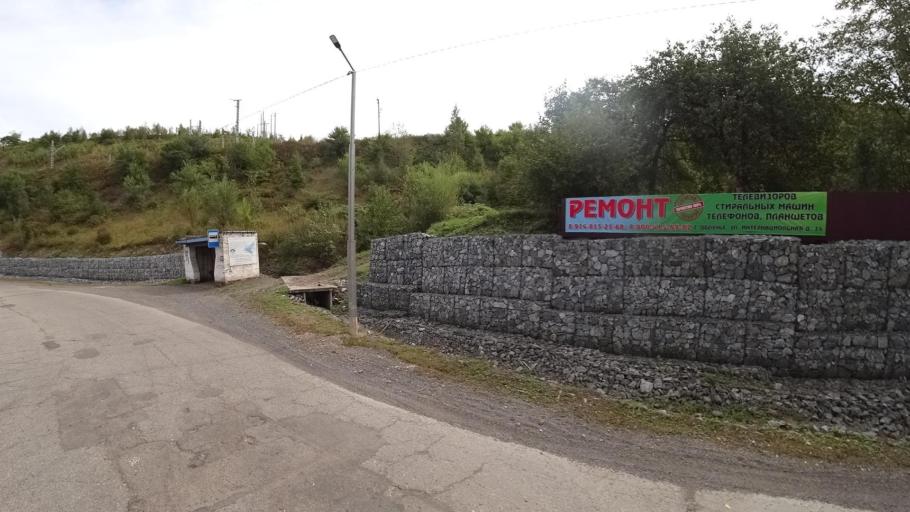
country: RU
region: Jewish Autonomous Oblast
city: Khingansk
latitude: 48.9963
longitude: 131.0567
